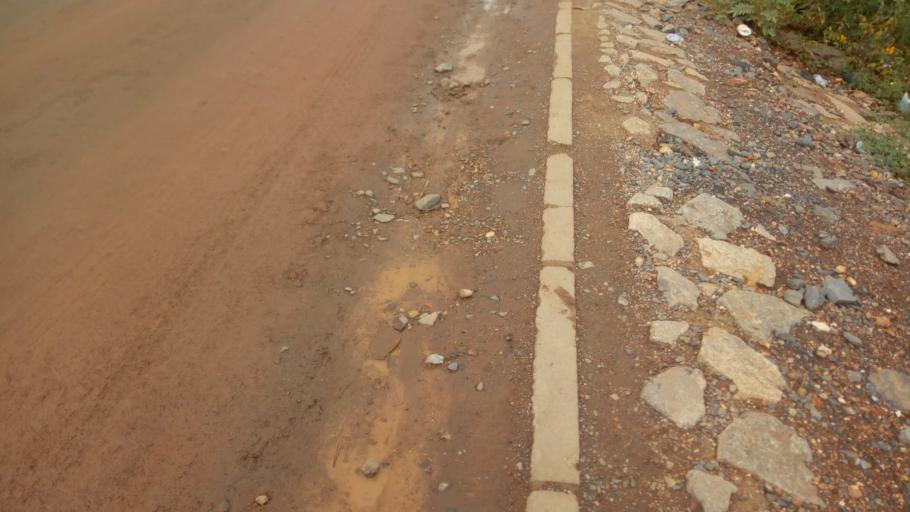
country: GH
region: Ashanti
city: Obuasi
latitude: 6.2107
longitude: -1.6905
